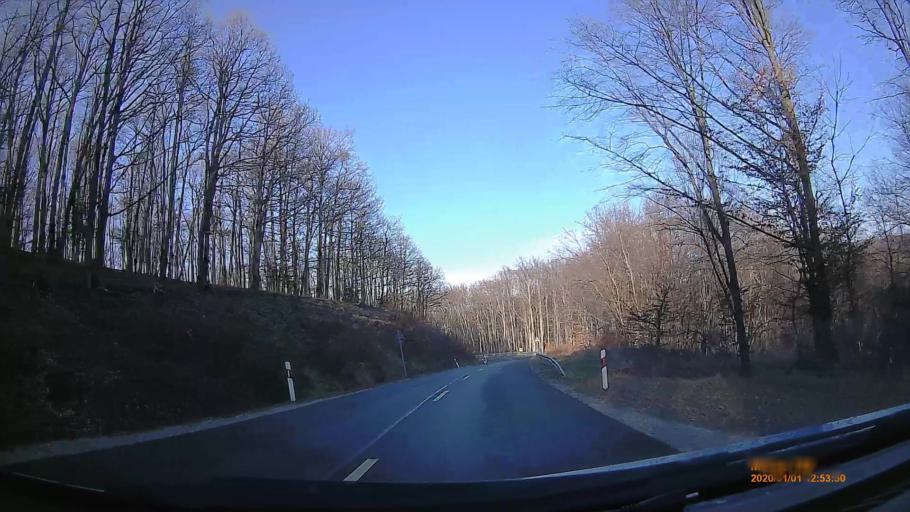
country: HU
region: Heves
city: Paradsasvar
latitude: 47.9064
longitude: 19.9923
